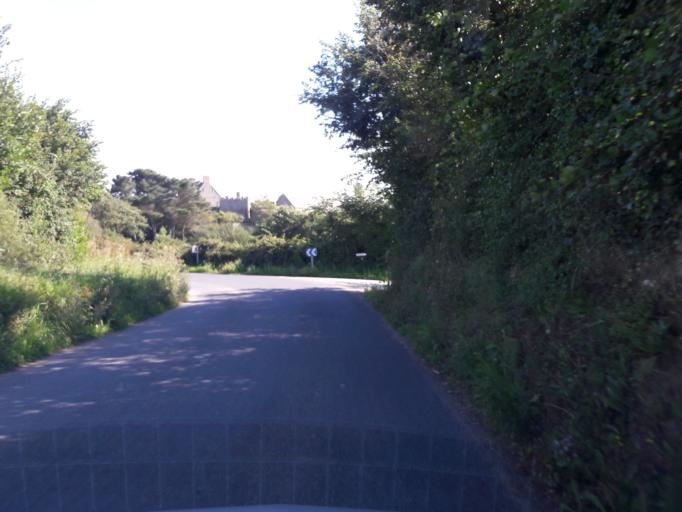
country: FR
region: Lower Normandy
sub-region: Departement de la Manche
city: Les Pieux
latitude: 49.4921
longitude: -1.8283
